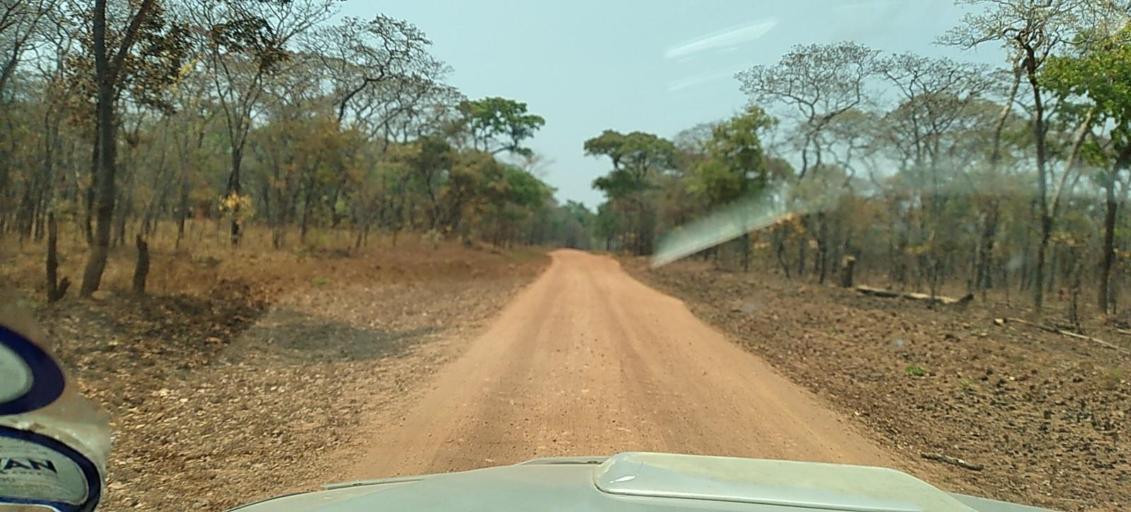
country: ZM
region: North-Western
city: Kasempa
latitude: -13.5621
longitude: 26.0853
